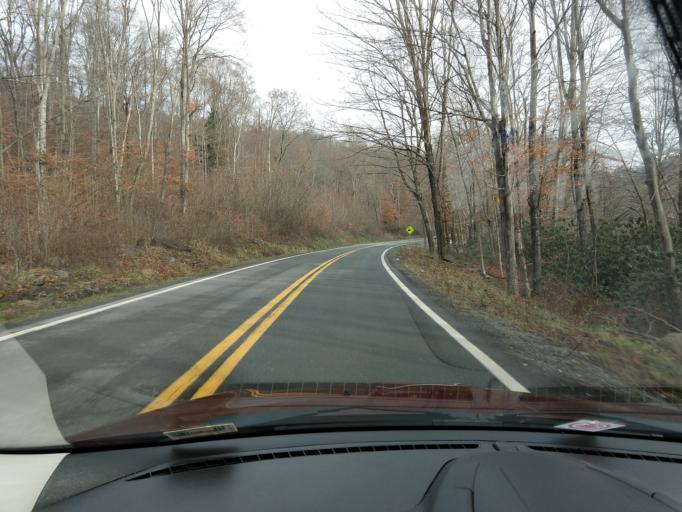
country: US
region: West Virginia
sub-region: Greenbrier County
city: Rainelle
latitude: 38.0912
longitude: -80.7051
